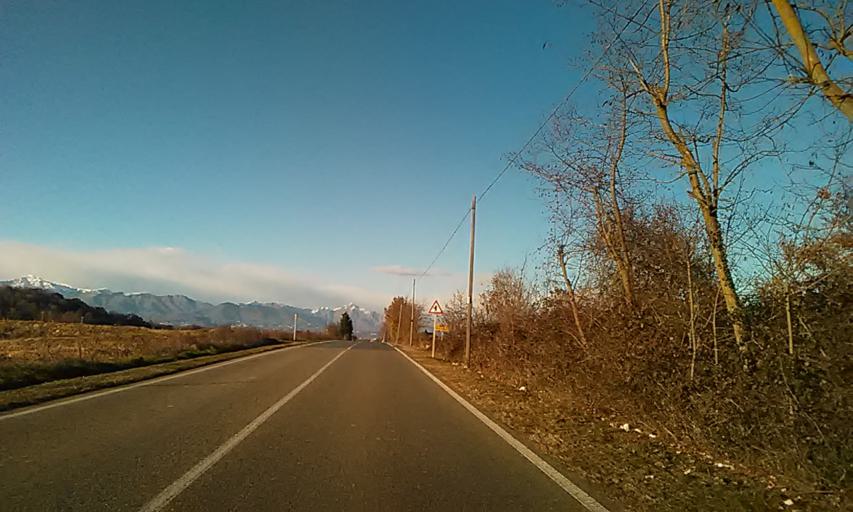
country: IT
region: Piedmont
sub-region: Provincia di Biella
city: Gifflenga
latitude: 45.4783
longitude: 8.2185
